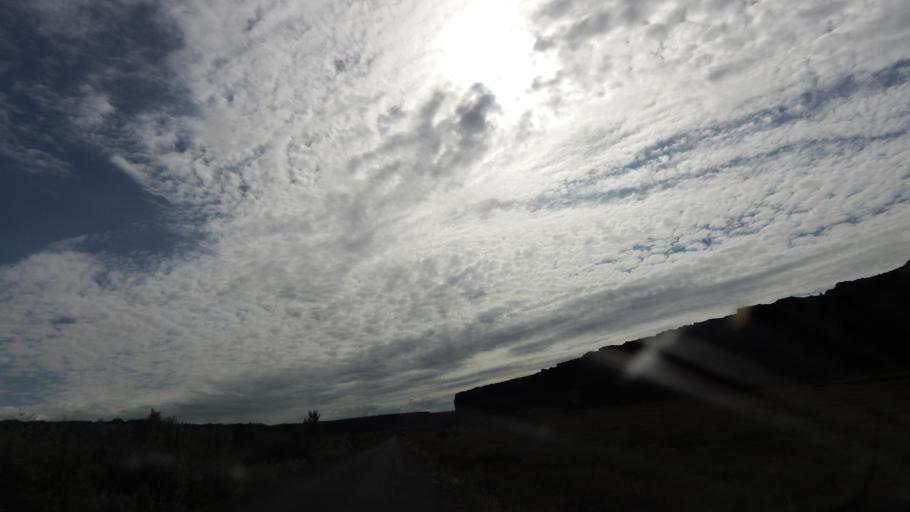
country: IS
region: Northeast
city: Husavik
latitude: 66.0223
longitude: -16.4954
